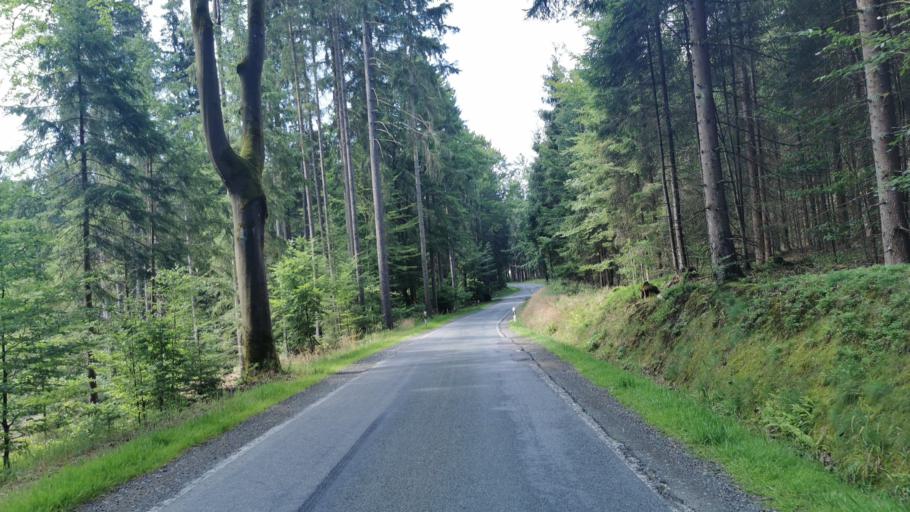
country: DE
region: Bavaria
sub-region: Upper Franconia
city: Tschirn
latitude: 50.3489
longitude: 11.4501
